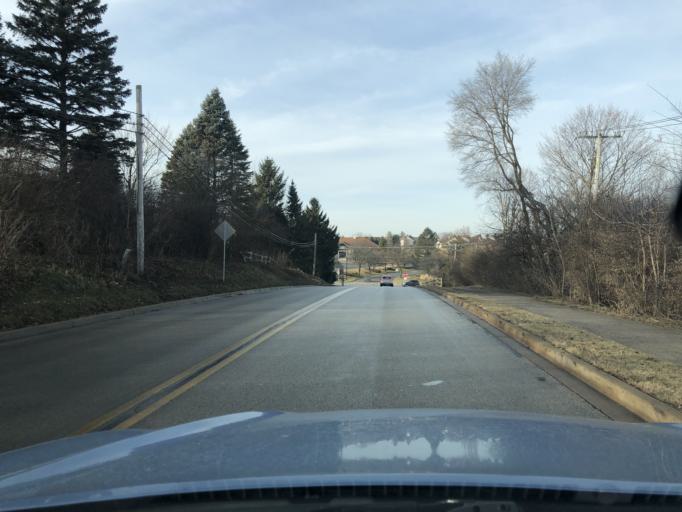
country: US
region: Illinois
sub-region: McHenry County
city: Algonquin
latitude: 42.1574
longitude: -88.3144
